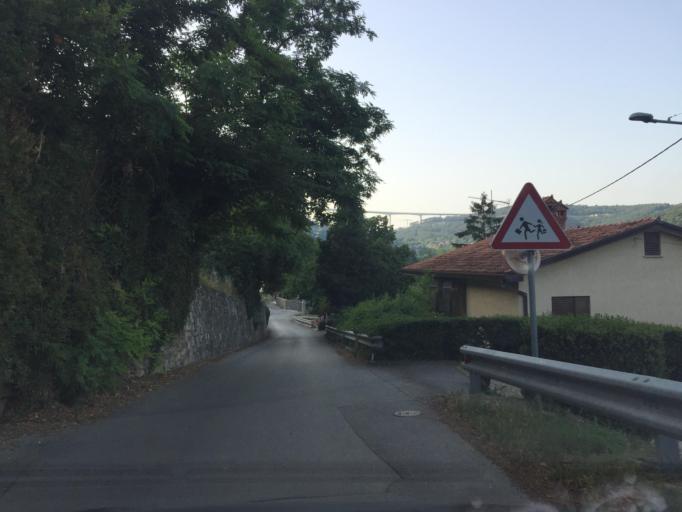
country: IT
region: Friuli Venezia Giulia
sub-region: Provincia di Trieste
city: Dolina
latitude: 45.5724
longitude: 13.8565
